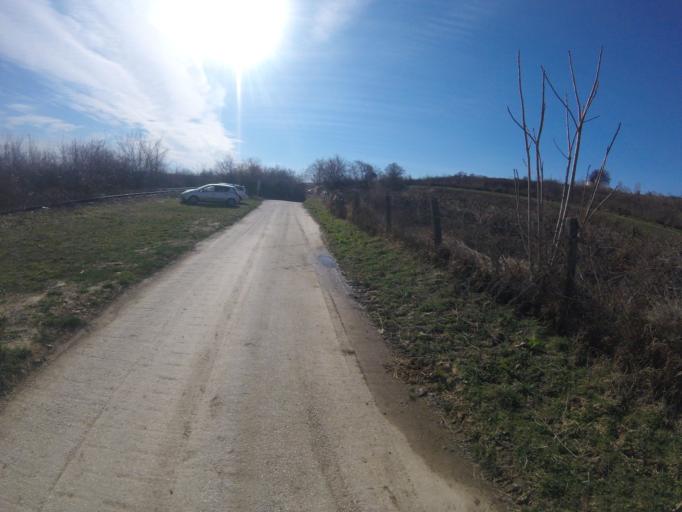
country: HU
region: Tolna
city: Bataszek
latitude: 46.1725
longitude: 18.7024
